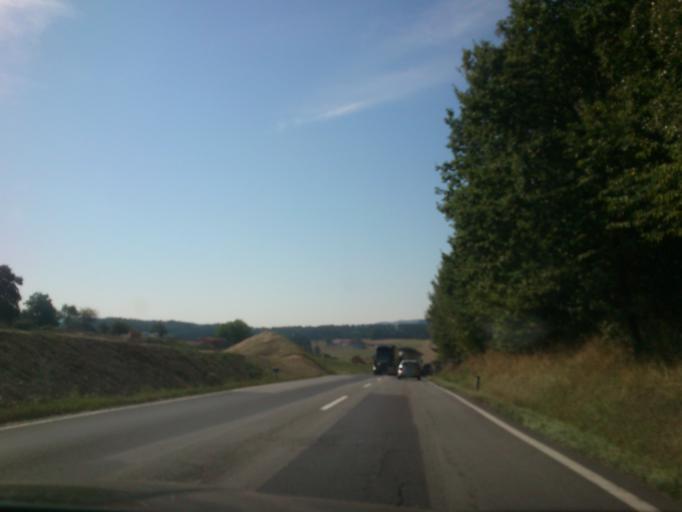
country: AT
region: Upper Austria
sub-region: Politischer Bezirk Freistadt
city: Freistadt
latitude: 48.4672
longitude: 14.5021
